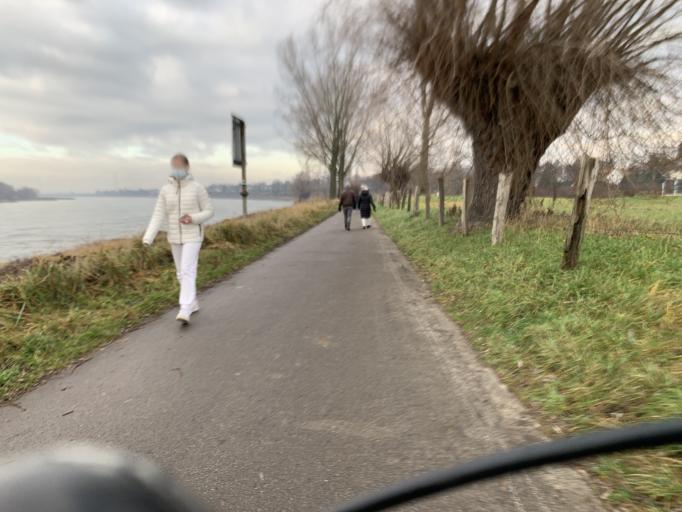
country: DE
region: North Rhine-Westphalia
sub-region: Regierungsbezirk Dusseldorf
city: Meerbusch
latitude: 51.3182
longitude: 6.7368
